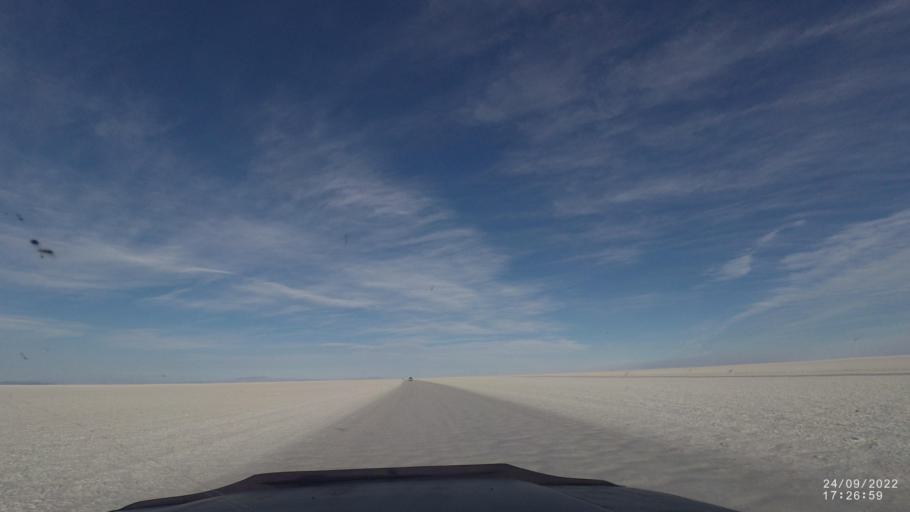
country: BO
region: Potosi
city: Colchani
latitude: -20.2981
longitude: -67.4580
